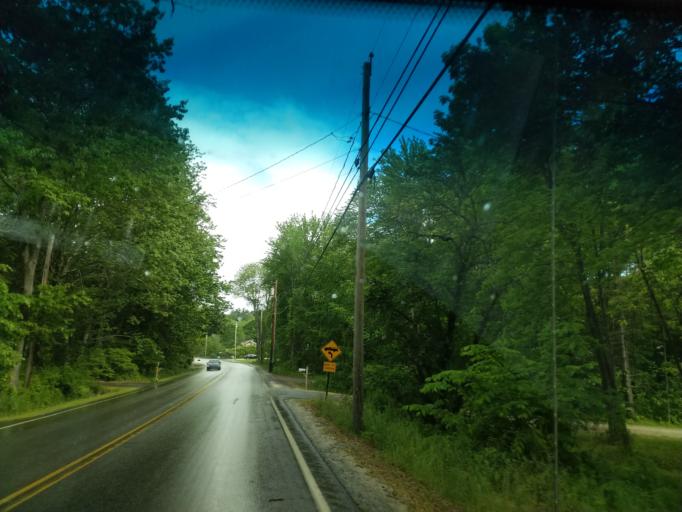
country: US
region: Maine
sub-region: Cumberland County
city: South Windham
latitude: 43.7930
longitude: -70.3586
